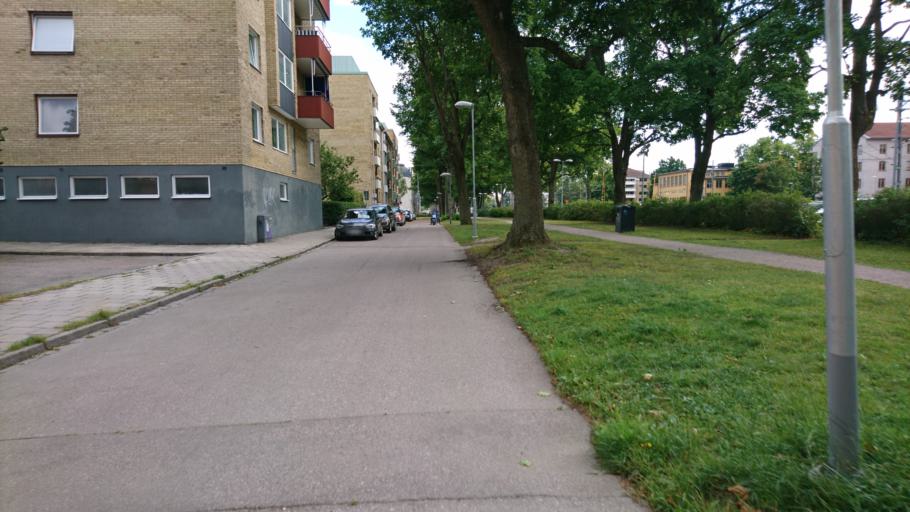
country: SE
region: Uppsala
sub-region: Uppsala Kommun
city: Uppsala
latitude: 59.8638
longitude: 17.6383
